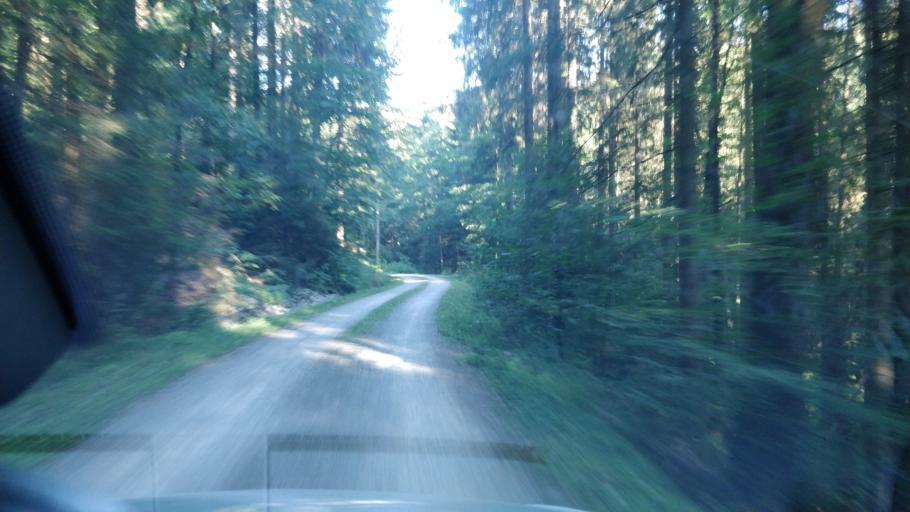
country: DE
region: Baden-Wuerttemberg
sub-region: Regierungsbezirk Stuttgart
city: Murrhardt
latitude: 49.0177
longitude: 9.5789
